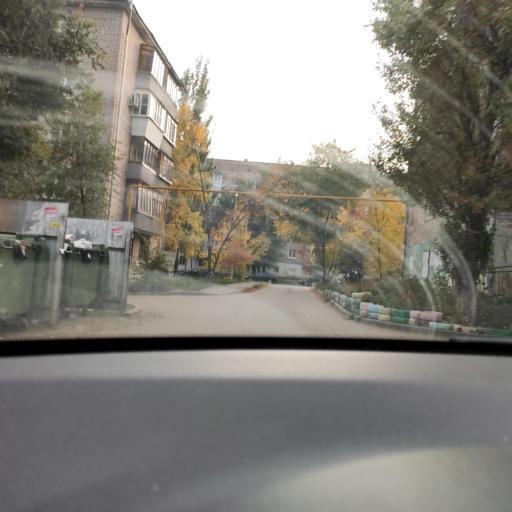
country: RU
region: Samara
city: Samara
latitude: 53.2147
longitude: 50.2399
